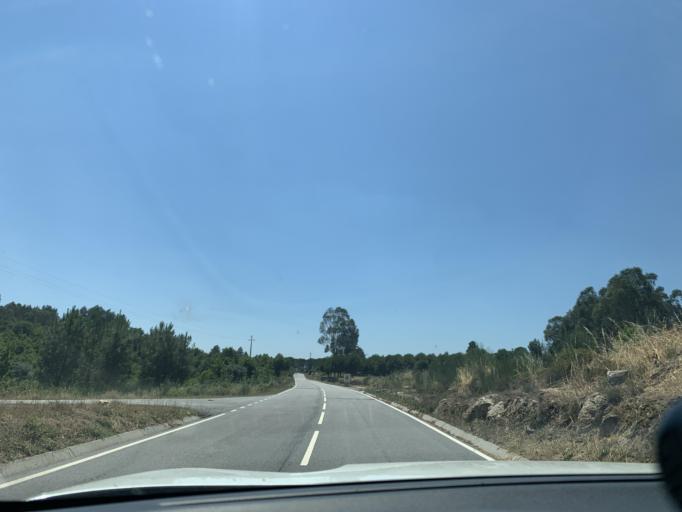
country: PT
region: Viseu
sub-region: Mangualde
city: Mangualde
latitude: 40.5655
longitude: -7.6801
